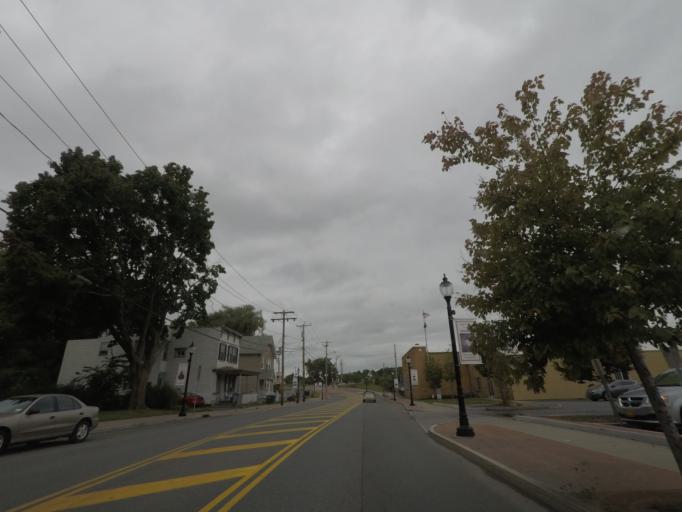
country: US
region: New York
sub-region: Rensselaer County
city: Rensselaer
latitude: 42.6430
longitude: -73.7429
